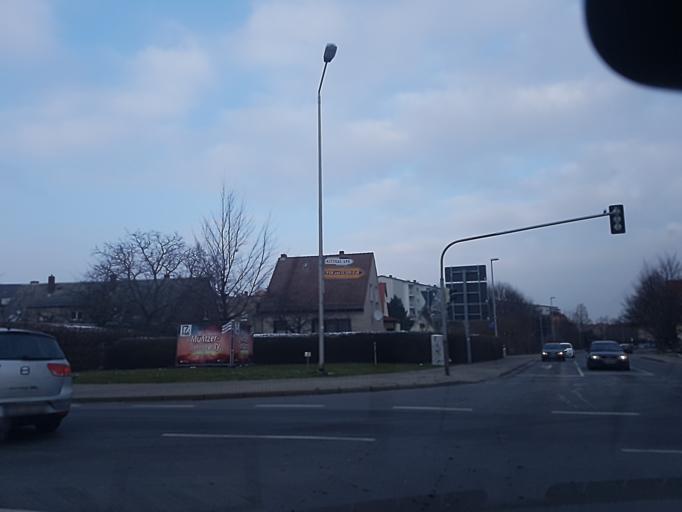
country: DE
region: Saxony
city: Oschatz
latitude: 51.3028
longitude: 13.0971
